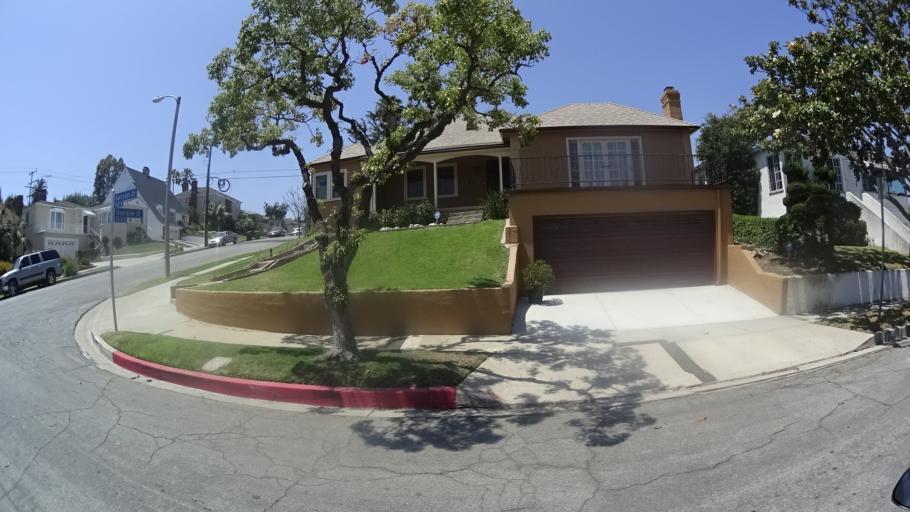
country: US
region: California
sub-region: Los Angeles County
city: View Park-Windsor Hills
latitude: 33.9927
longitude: -118.3529
